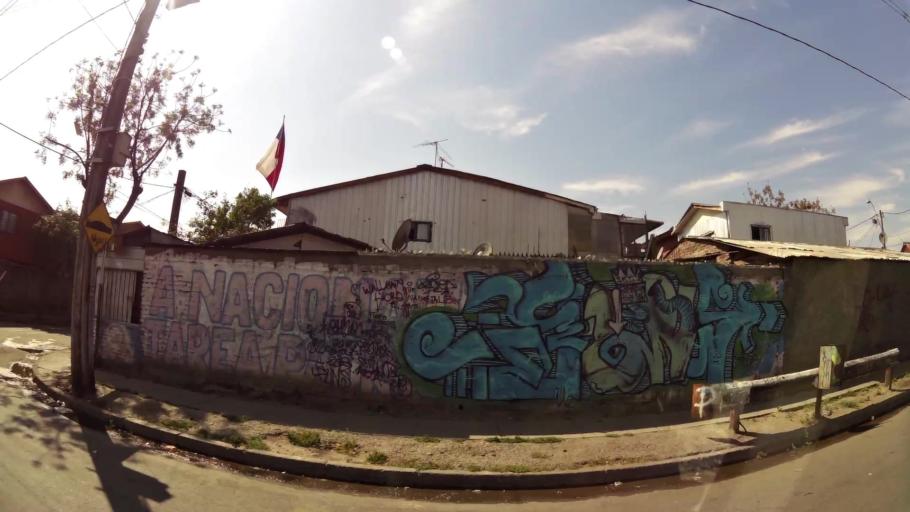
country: CL
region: Santiago Metropolitan
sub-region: Provincia de Santiago
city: La Pintana
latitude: -33.5617
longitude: -70.6520
